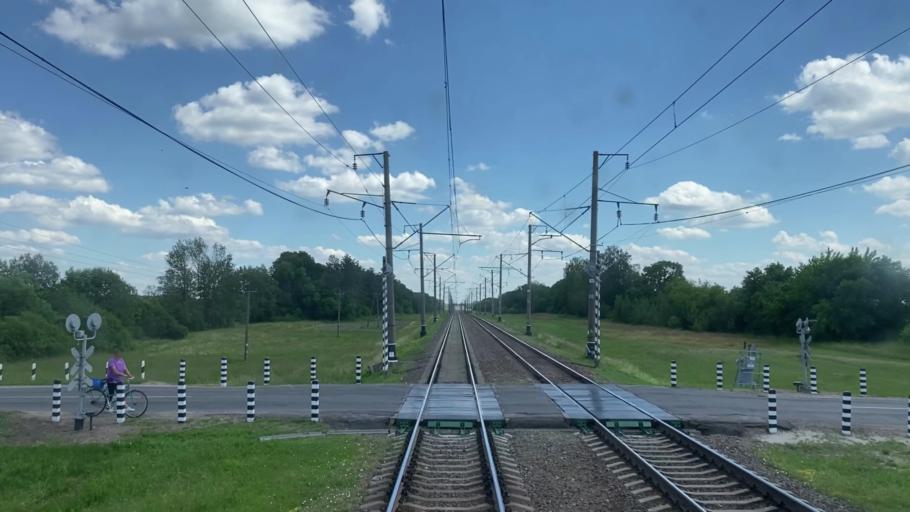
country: BY
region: Brest
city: Ivatsevichy
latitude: 52.8337
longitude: 25.4975
